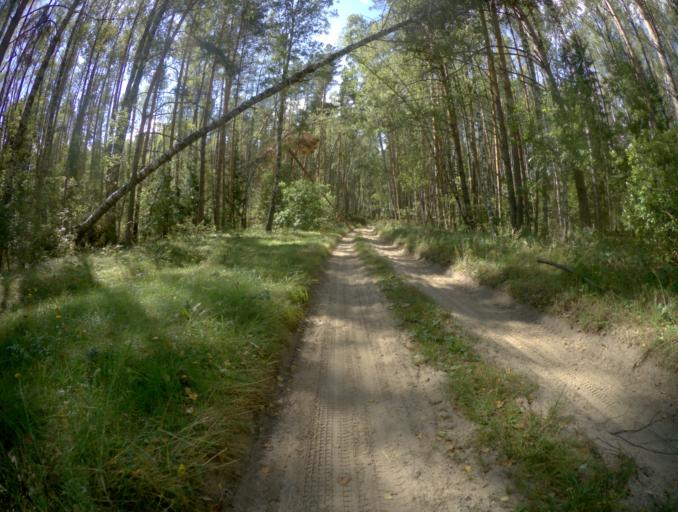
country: RU
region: Vladimir
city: Krasnaya Gorbatka
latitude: 55.8732
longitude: 41.8506
